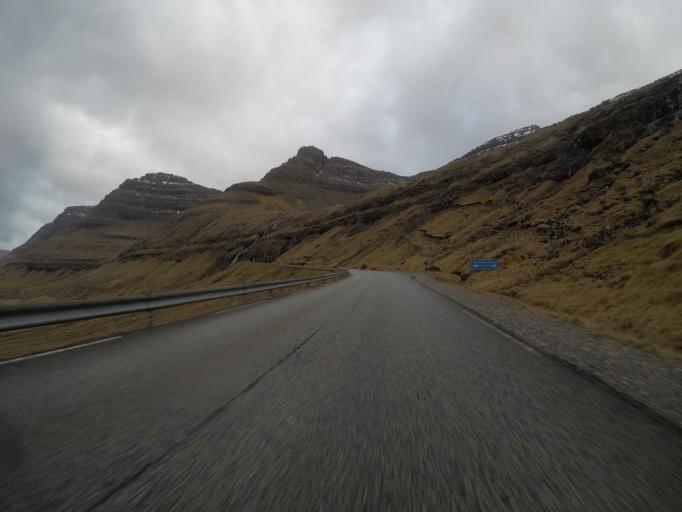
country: FO
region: Nordoyar
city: Klaksvik
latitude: 62.2773
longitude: -6.5233
